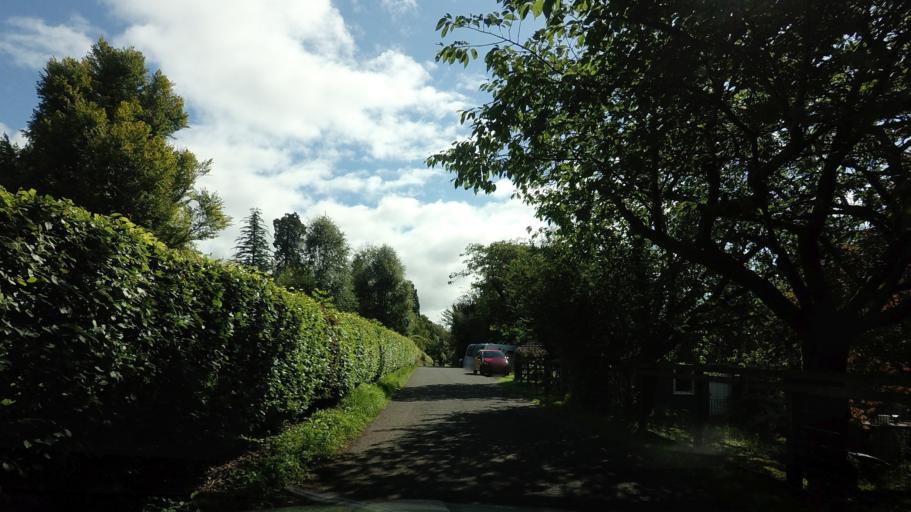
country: GB
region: Scotland
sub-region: Stirling
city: Killearn
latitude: 56.0642
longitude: -4.4704
